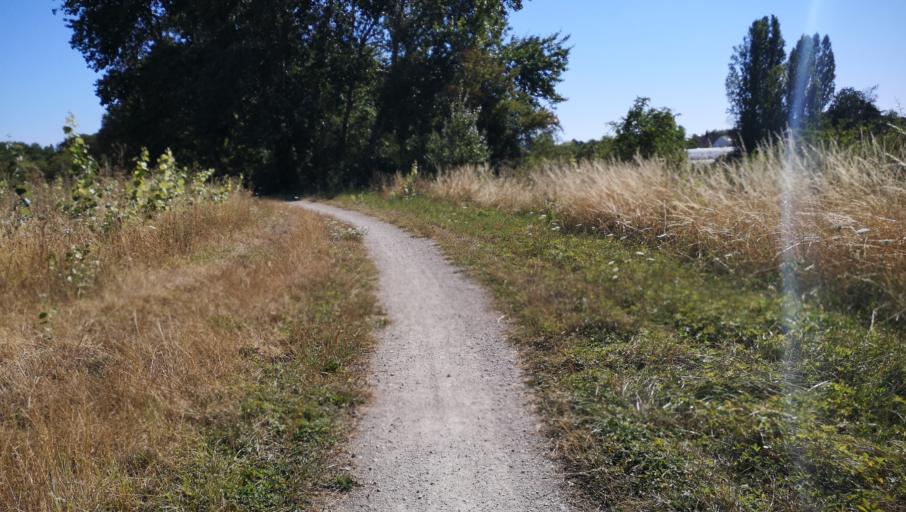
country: FR
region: Centre
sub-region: Departement du Loiret
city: Semoy
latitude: 47.9326
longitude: 1.9582
